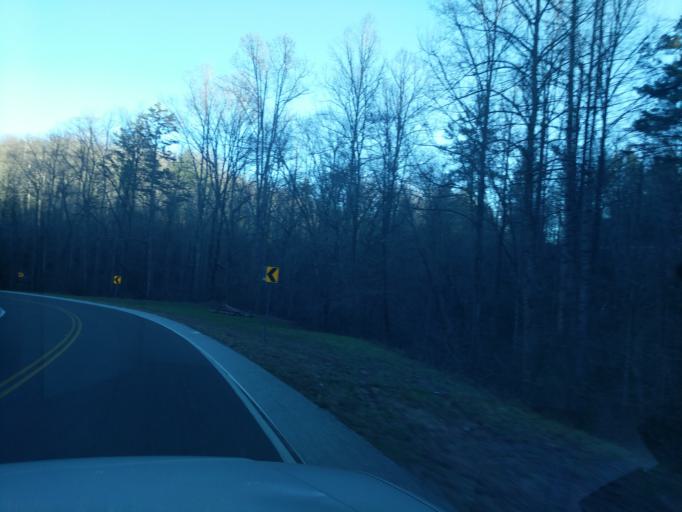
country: US
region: Georgia
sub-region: Rabun County
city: Clayton
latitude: 34.8134
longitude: -83.3194
